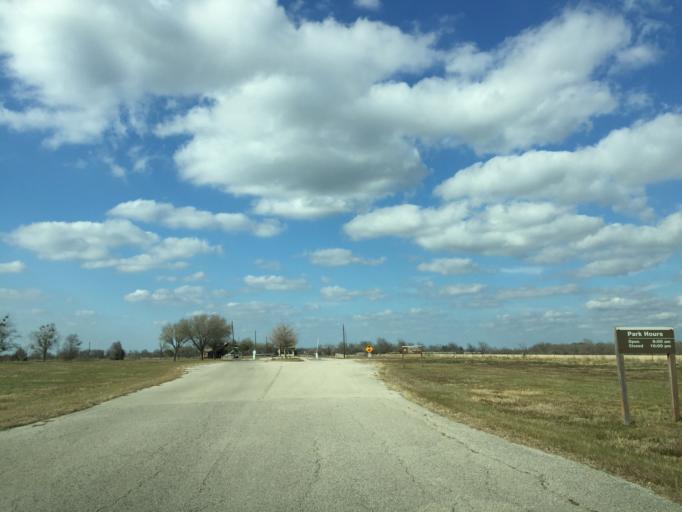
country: US
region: Texas
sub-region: Williamson County
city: Granger
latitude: 30.6645
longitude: -97.3647
